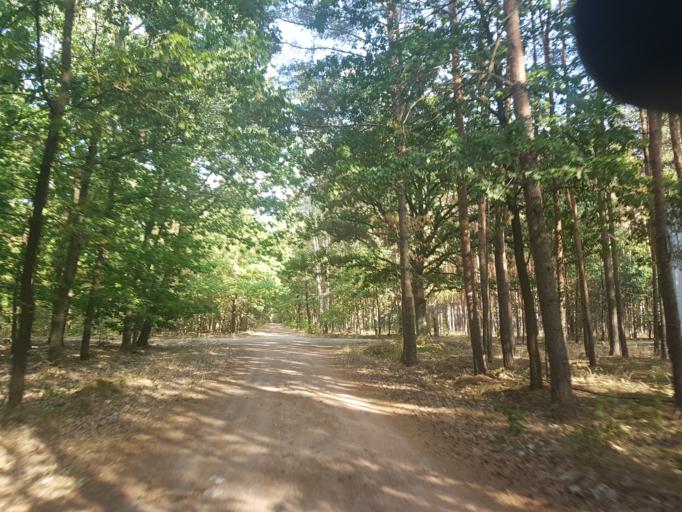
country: DE
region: Saxony-Anhalt
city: Jessen
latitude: 51.8648
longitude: 13.0336
